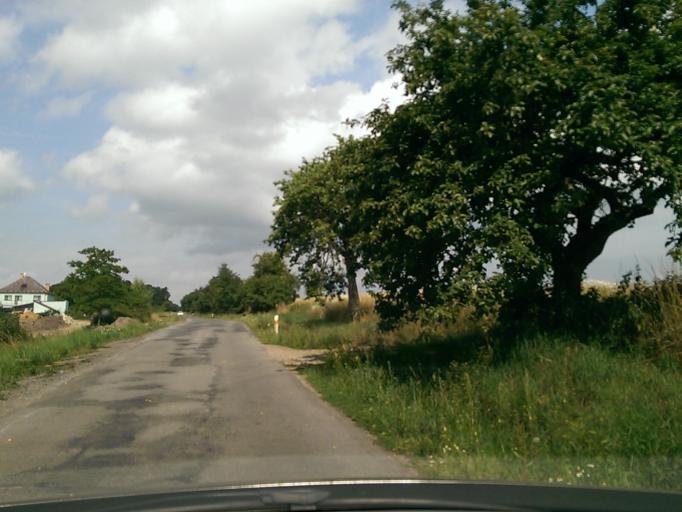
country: CZ
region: Central Bohemia
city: Bakov nad Jizerou
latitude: 50.4780
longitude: 14.9225
